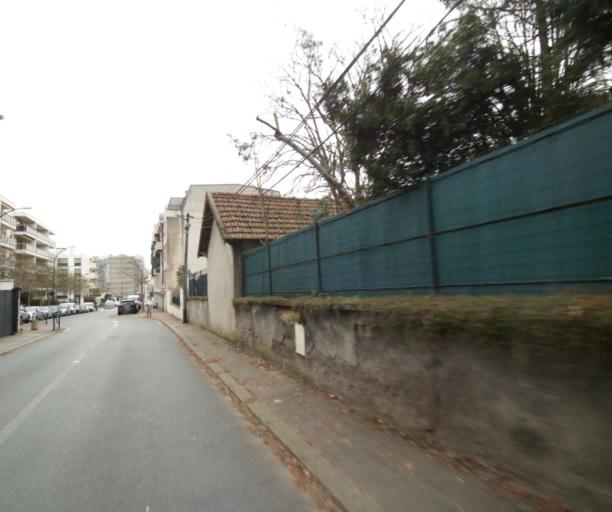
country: FR
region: Ile-de-France
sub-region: Departement des Hauts-de-Seine
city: Garches
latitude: 48.8403
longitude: 2.1810
